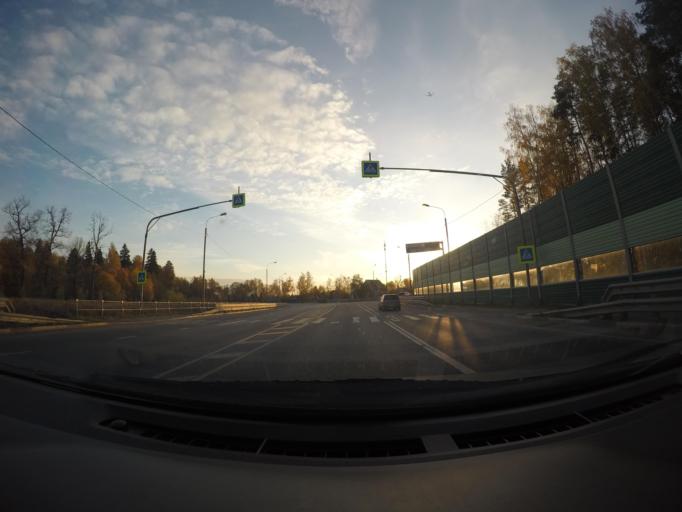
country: RU
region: Moskovskaya
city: Firsanovka
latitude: 55.9503
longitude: 37.2533
